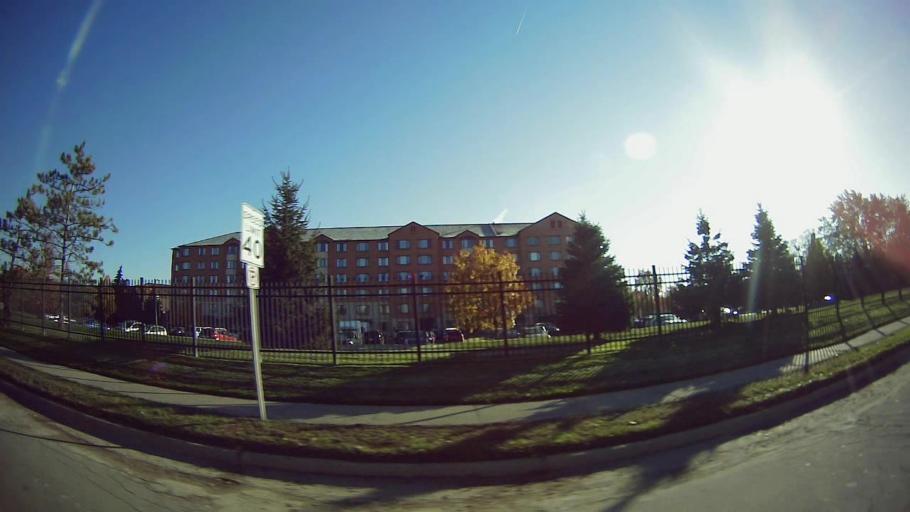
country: US
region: Michigan
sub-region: Wayne County
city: Dearborn
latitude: 42.3264
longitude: -83.1955
